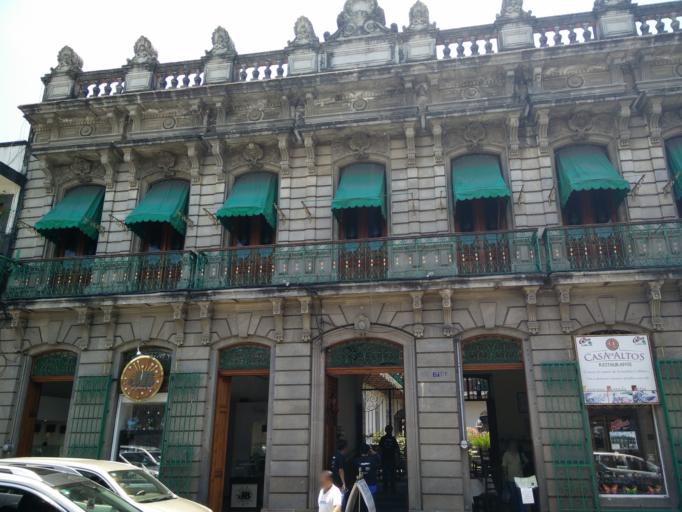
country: MX
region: Veracruz
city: Coatepec
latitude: 19.4540
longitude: -96.9574
